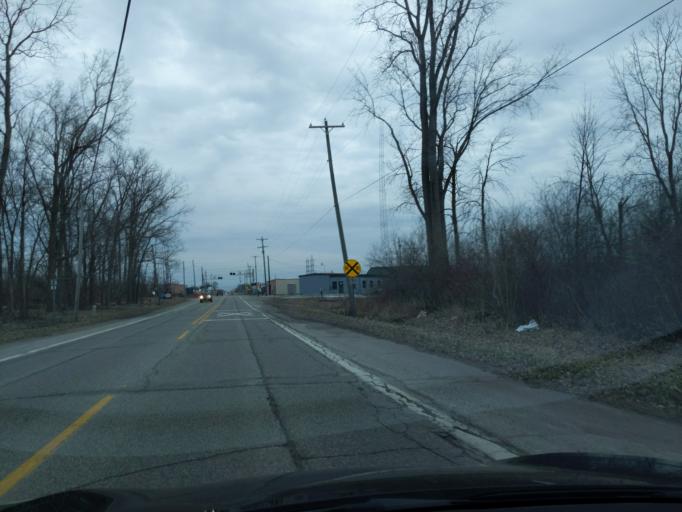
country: US
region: Michigan
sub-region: Bay County
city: Bay City
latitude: 43.6323
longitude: -83.9140
